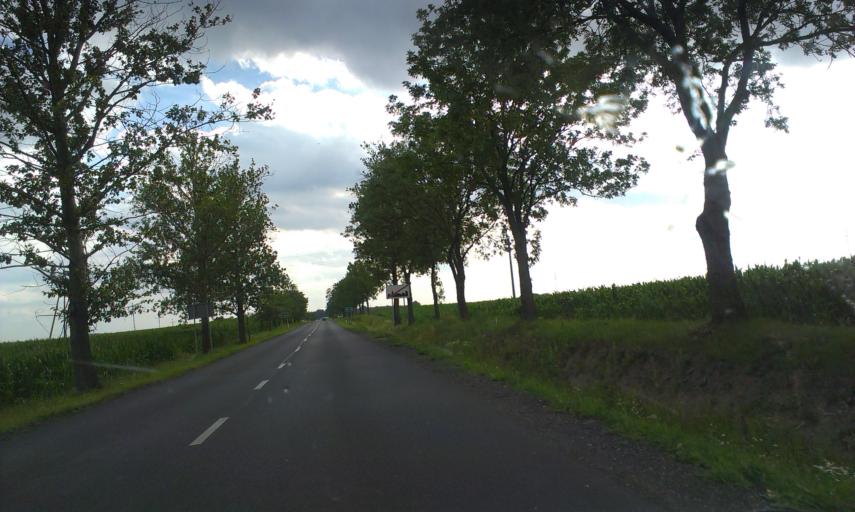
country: PL
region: Greater Poland Voivodeship
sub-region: Powiat zlotowski
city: Krajenka
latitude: 53.3321
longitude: 17.0077
